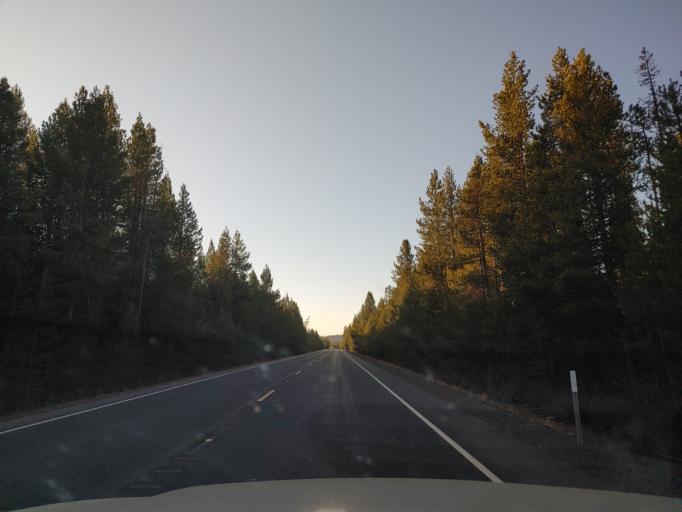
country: US
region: Oregon
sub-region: Deschutes County
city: La Pine
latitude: 43.4100
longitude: -121.8305
